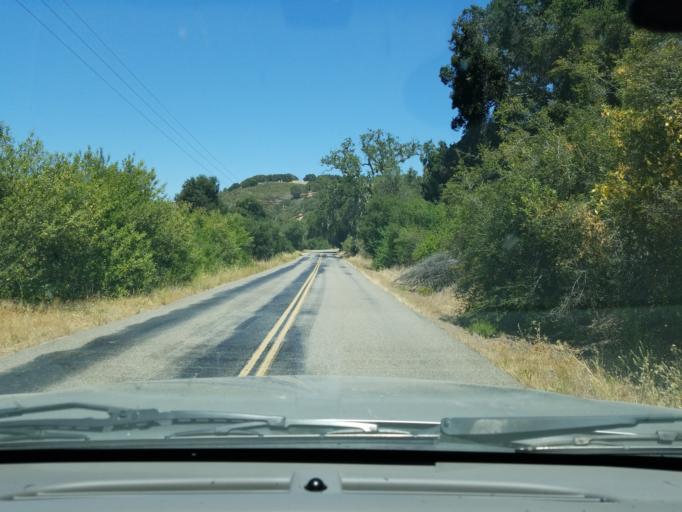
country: US
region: California
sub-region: Monterey County
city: Carmel Valley Village
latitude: 36.4341
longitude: -121.6288
